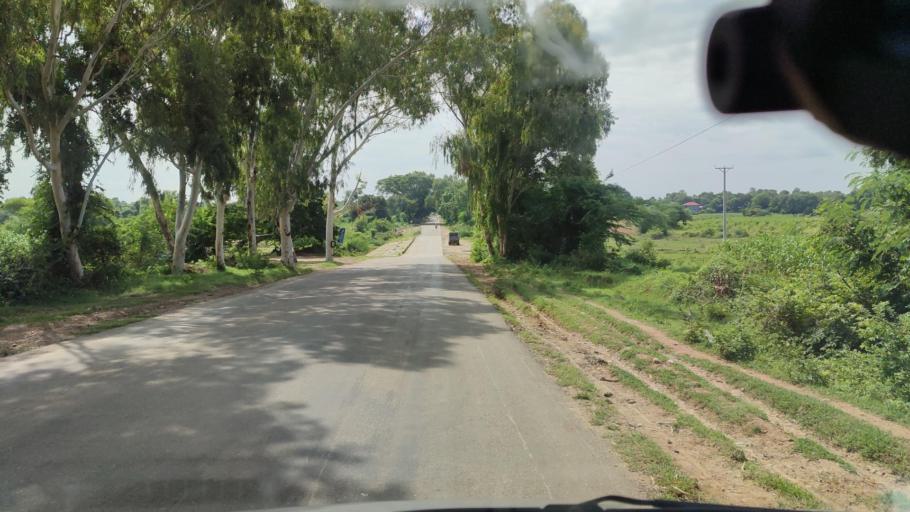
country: MM
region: Mandalay
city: Meiktila
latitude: 20.9761
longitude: 95.7393
